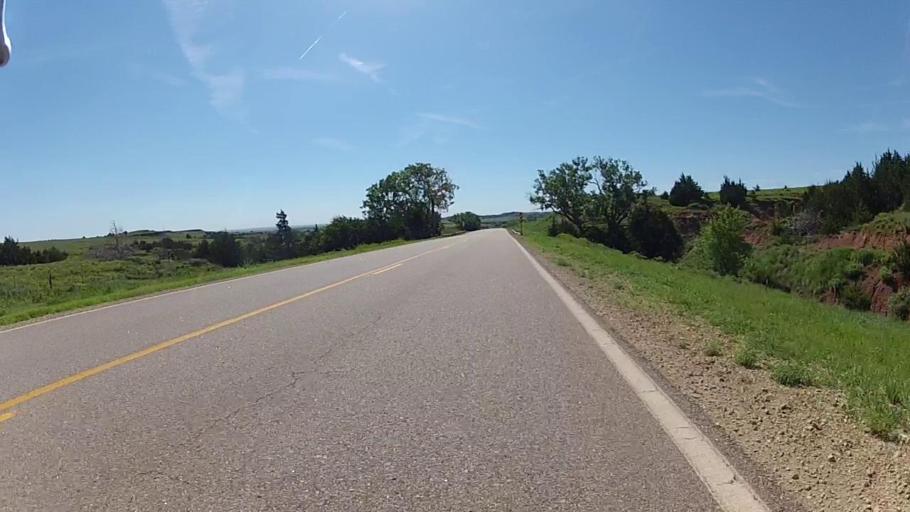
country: US
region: Kansas
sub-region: Barber County
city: Medicine Lodge
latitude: 37.2777
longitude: -98.7378
